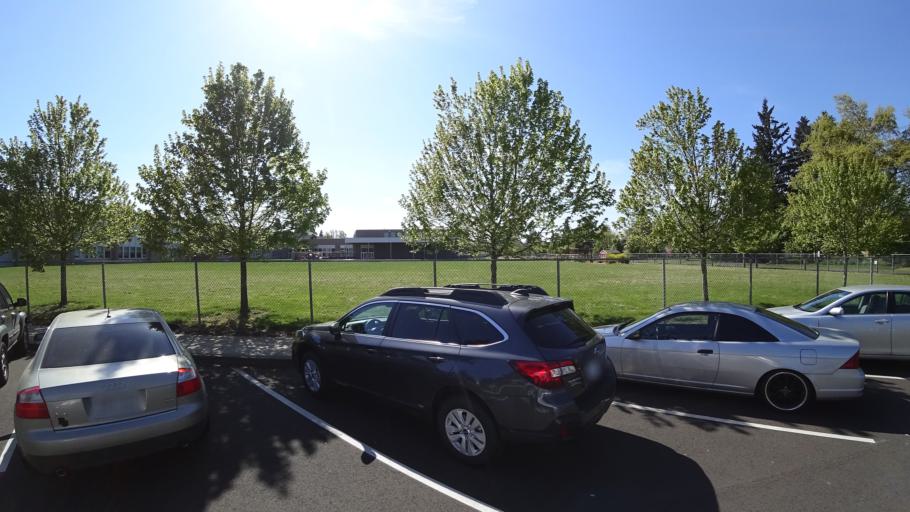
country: US
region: Oregon
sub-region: Washington County
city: Hillsboro
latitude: 45.5246
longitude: -122.9755
